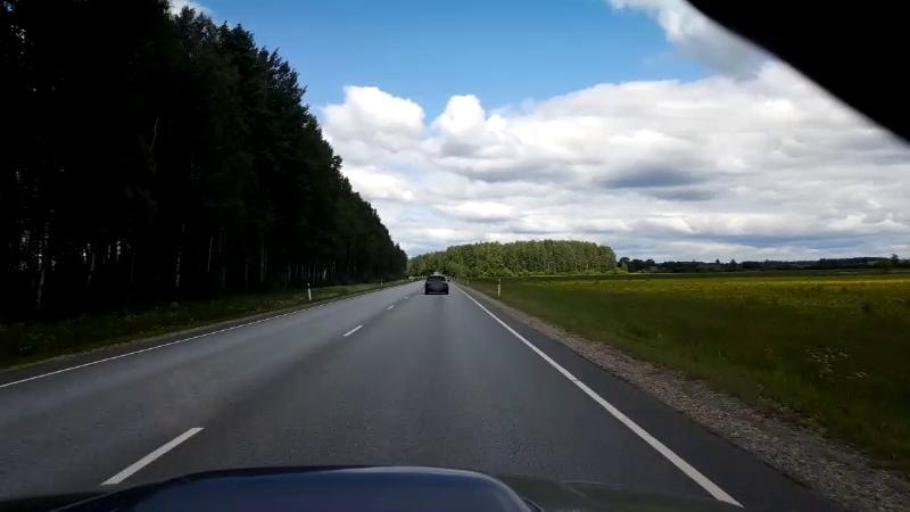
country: EE
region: Paernumaa
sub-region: Sauga vald
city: Sauga
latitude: 58.4699
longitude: 24.5239
